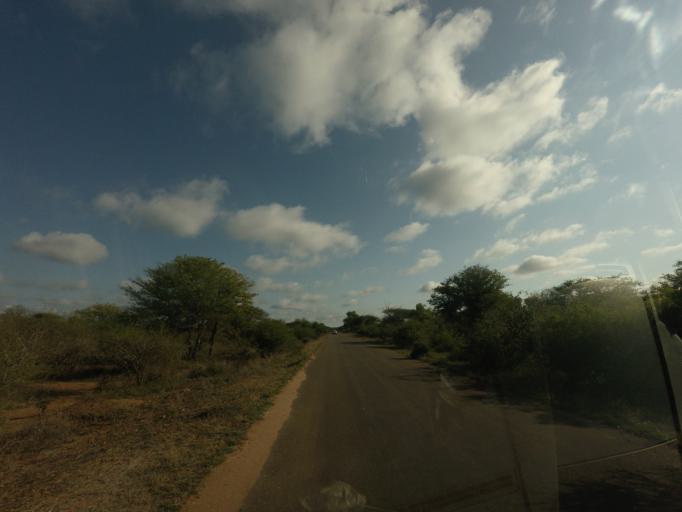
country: ZA
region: Mpumalanga
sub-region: Ehlanzeni District
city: Komatipoort
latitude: -25.2525
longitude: 31.8469
